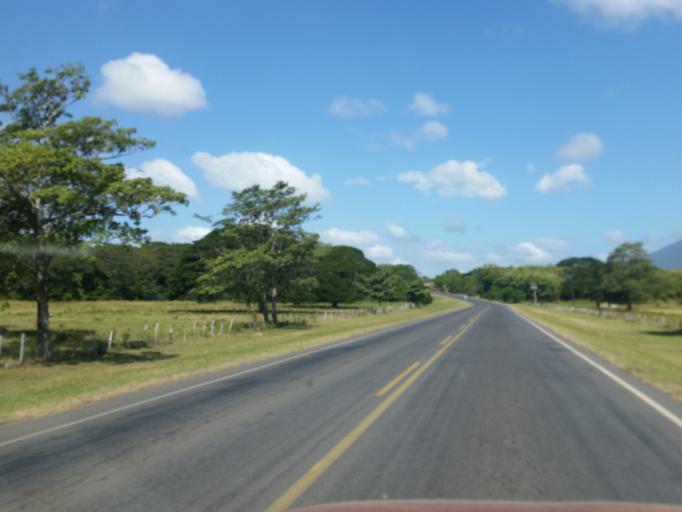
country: NI
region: Granada
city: Nandaime
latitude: 11.7215
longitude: -86.0124
